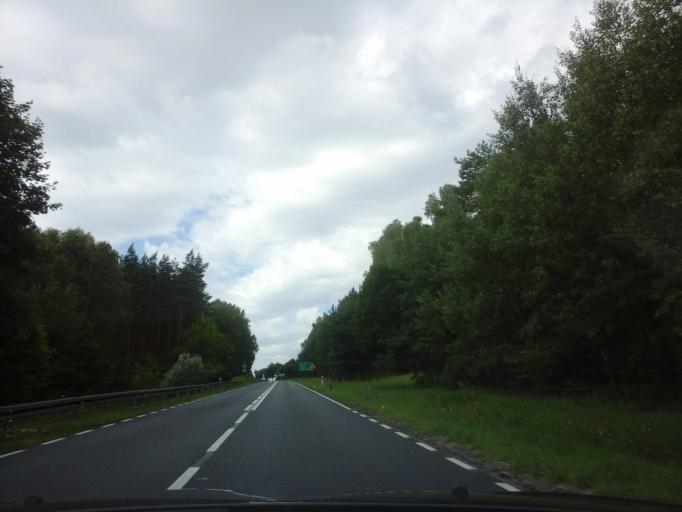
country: PL
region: West Pomeranian Voivodeship
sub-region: Powiat choszczenski
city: Recz
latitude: 53.2612
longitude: 15.5336
